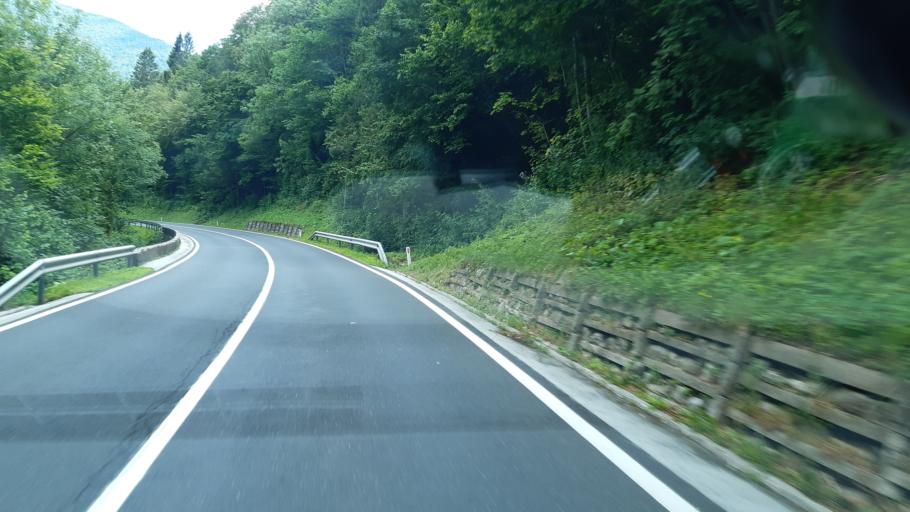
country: SI
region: Trzic
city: Trzic
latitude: 46.3777
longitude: 14.2964
